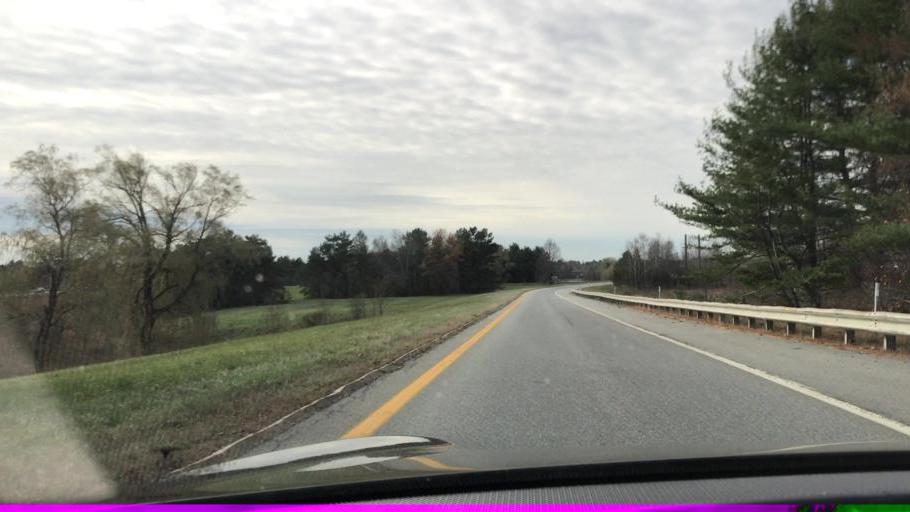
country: US
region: Maine
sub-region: Penobscot County
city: Bangor
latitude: 44.7906
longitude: -68.8067
